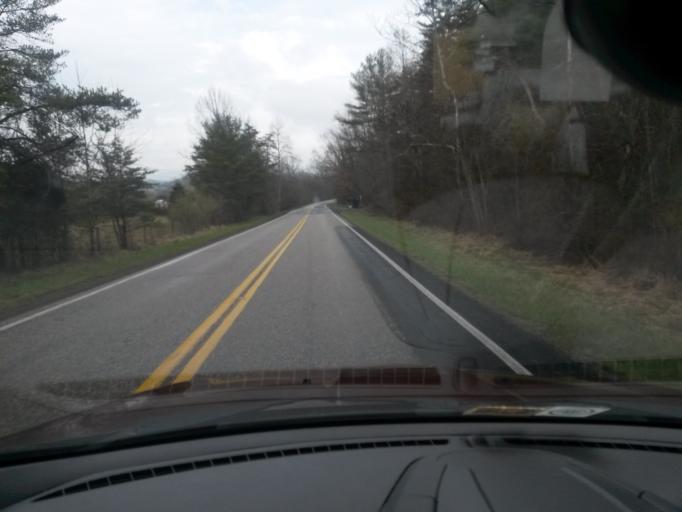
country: US
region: Virginia
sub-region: Bath County
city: Warm Springs
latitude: 37.9624
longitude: -79.6779
